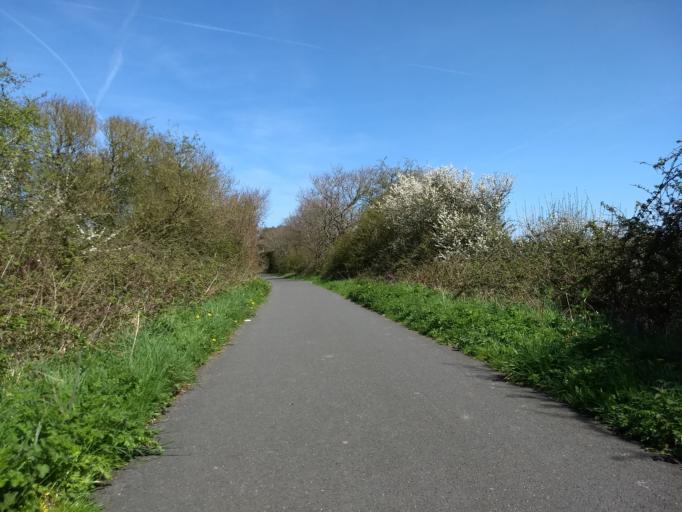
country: GB
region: England
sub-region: Isle of Wight
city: Newport
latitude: 50.7267
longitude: -1.2857
